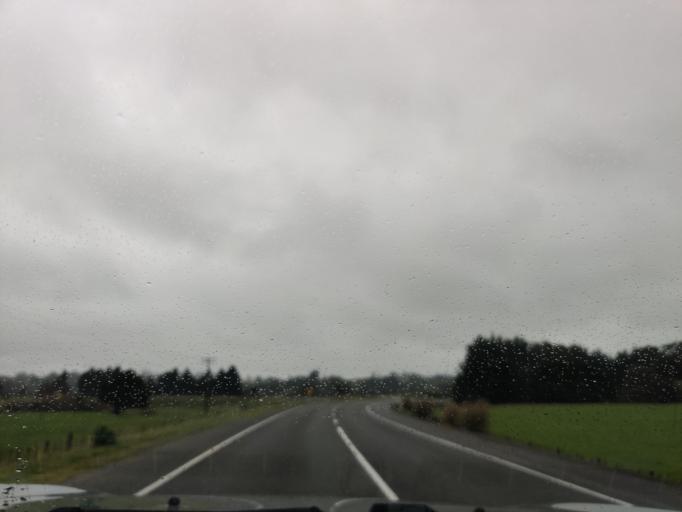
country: NZ
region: Manawatu-Wanganui
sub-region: Palmerston North City
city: Palmerston North
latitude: -40.0565
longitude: 176.2297
